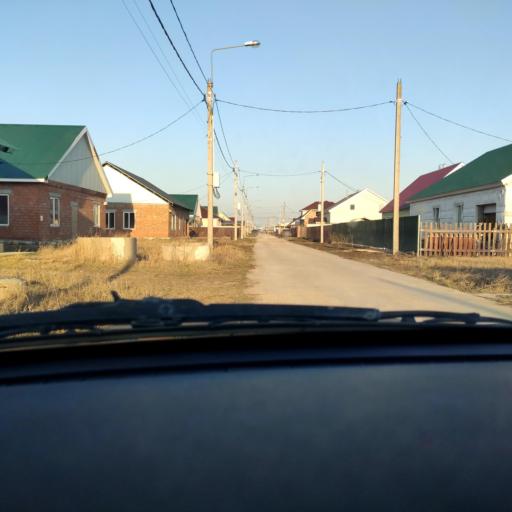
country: RU
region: Samara
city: Podstepki
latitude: 53.5758
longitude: 49.1124
